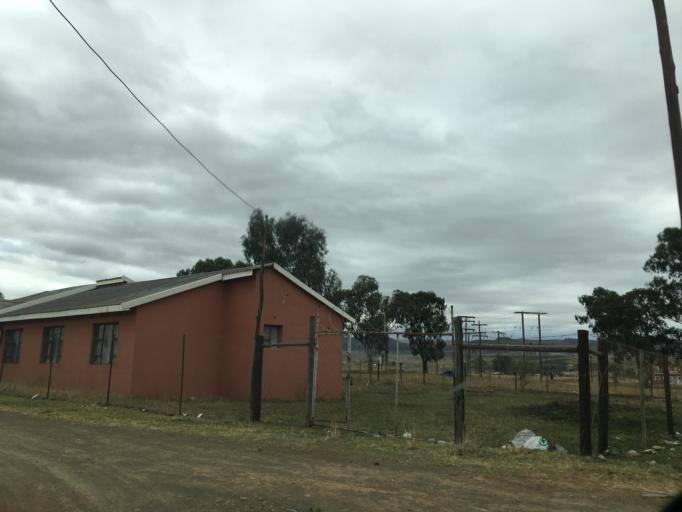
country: ZA
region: Eastern Cape
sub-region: Chris Hani District Municipality
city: Cala
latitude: -31.5338
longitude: 27.6903
